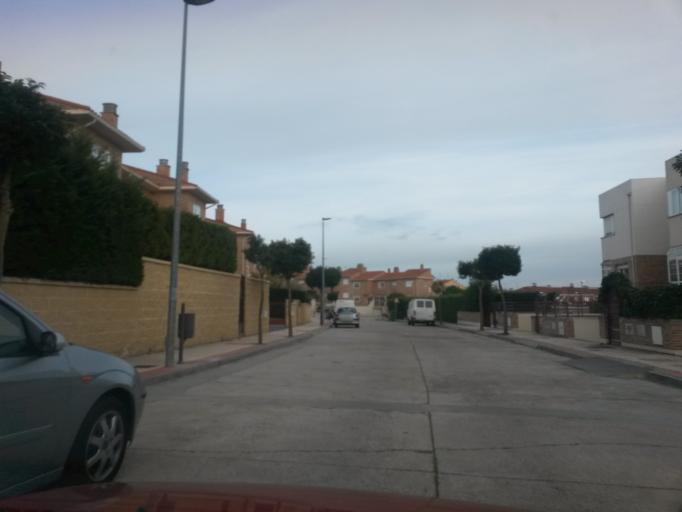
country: ES
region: Castille and Leon
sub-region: Provincia de Salamanca
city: Cabrerizos
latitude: 40.9810
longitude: -5.6084
